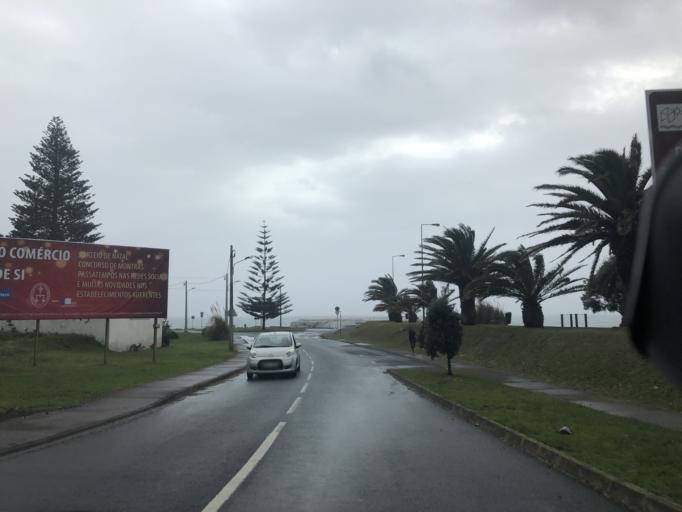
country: PT
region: Azores
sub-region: Ponta Delgada
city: Rosto de Cao
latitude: 37.7515
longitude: -25.6220
